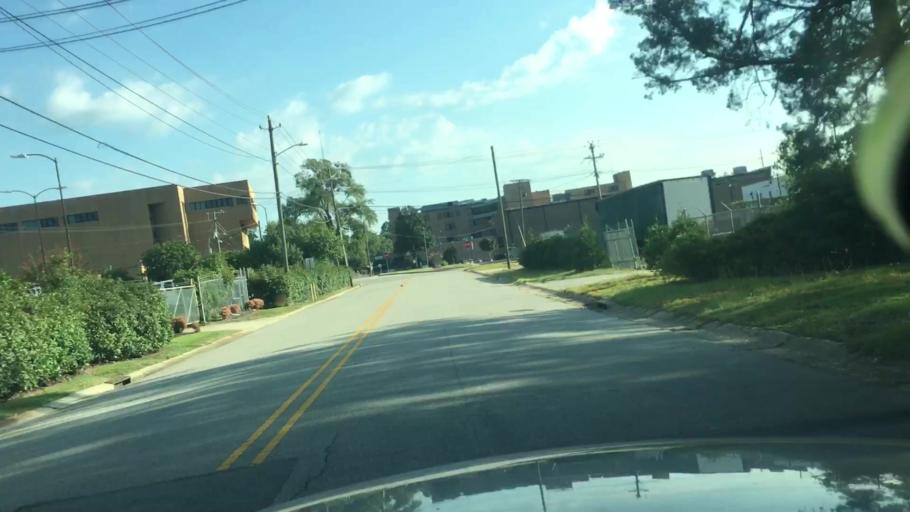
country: US
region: North Carolina
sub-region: Cumberland County
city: Fayetteville
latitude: 35.0521
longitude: -78.8896
